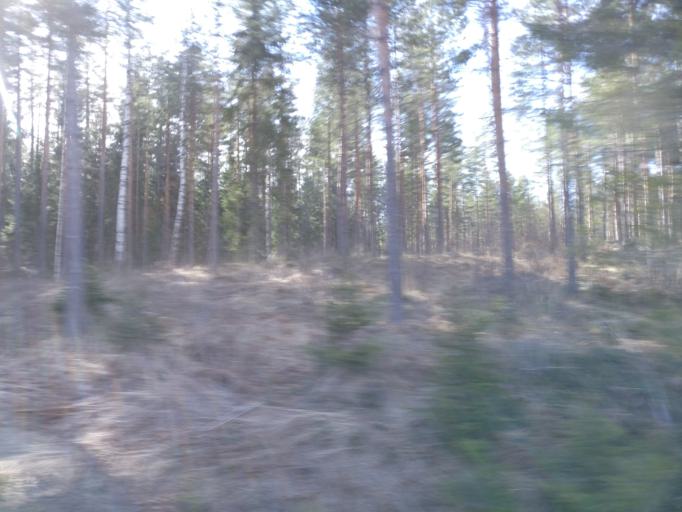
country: FI
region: Varsinais-Suomi
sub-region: Salo
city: Suomusjaervi
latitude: 60.3313
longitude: 23.6490
